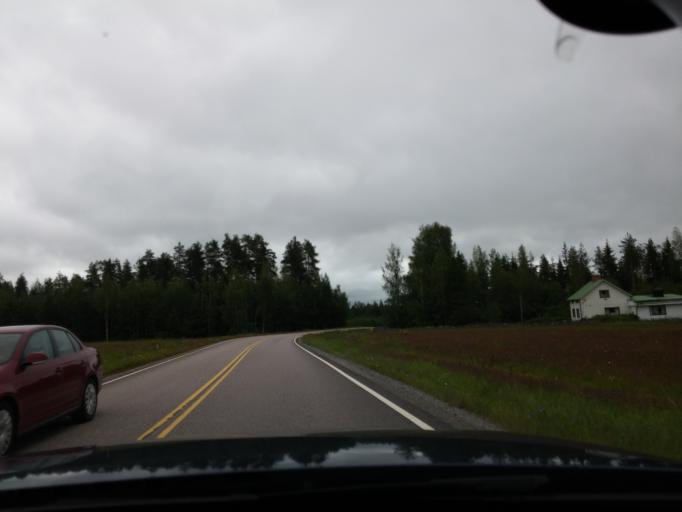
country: FI
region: Central Finland
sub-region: Saarijaervi-Viitasaari
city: Pylkoenmaeki
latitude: 62.6254
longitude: 24.7838
